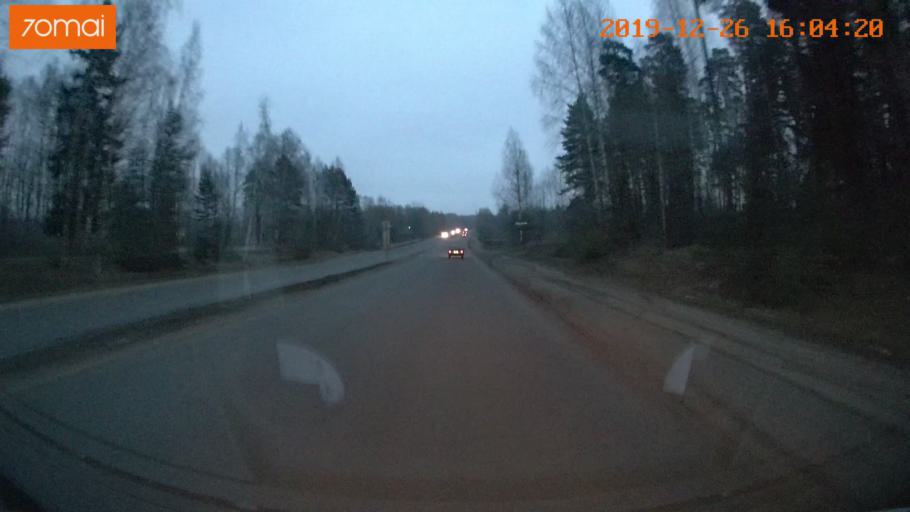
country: RU
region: Jaroslavl
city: Rybinsk
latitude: 58.0084
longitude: 38.8676
